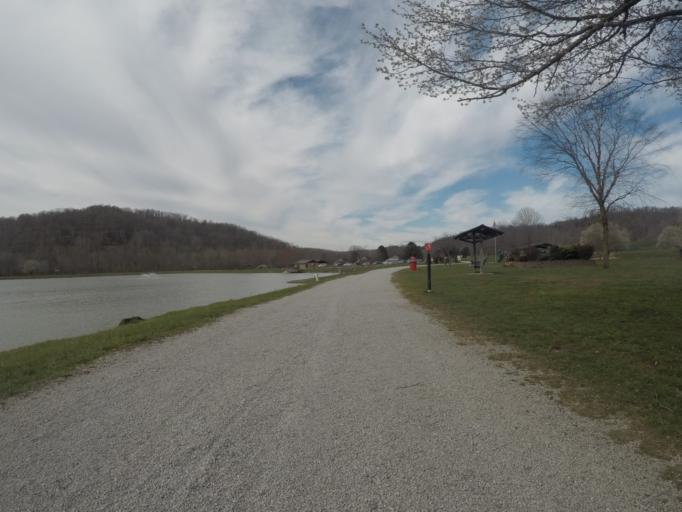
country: US
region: West Virginia
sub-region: Cabell County
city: Barboursville
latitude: 38.3881
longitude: -82.2981
